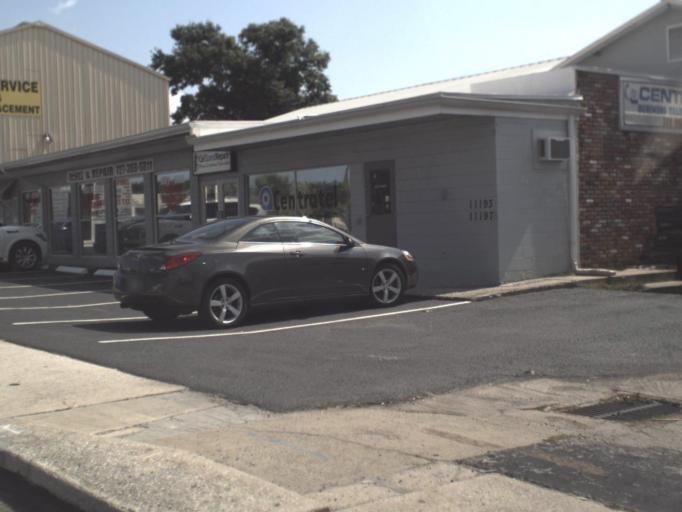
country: US
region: Florida
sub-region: Pinellas County
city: Ridgecrest
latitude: 27.8743
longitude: -82.7869
